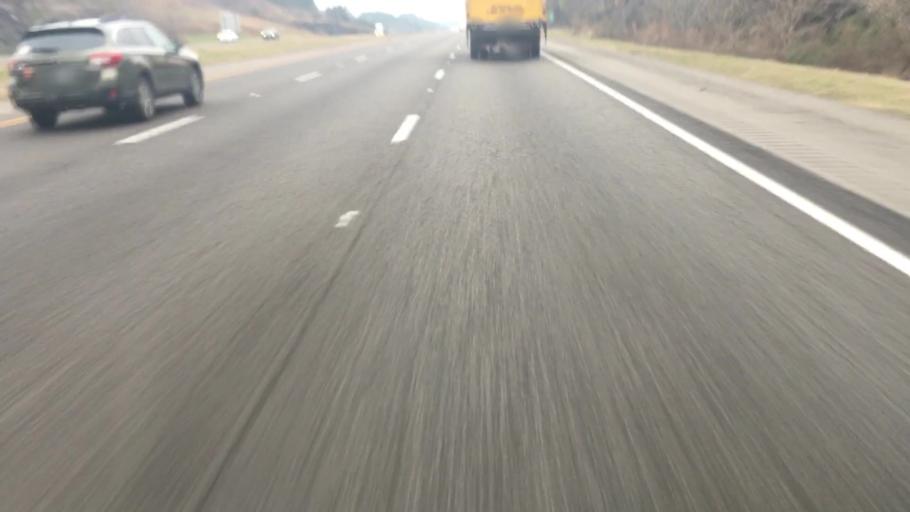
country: US
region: Alabama
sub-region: Jefferson County
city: Adamsville
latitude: 33.6214
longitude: -86.9428
